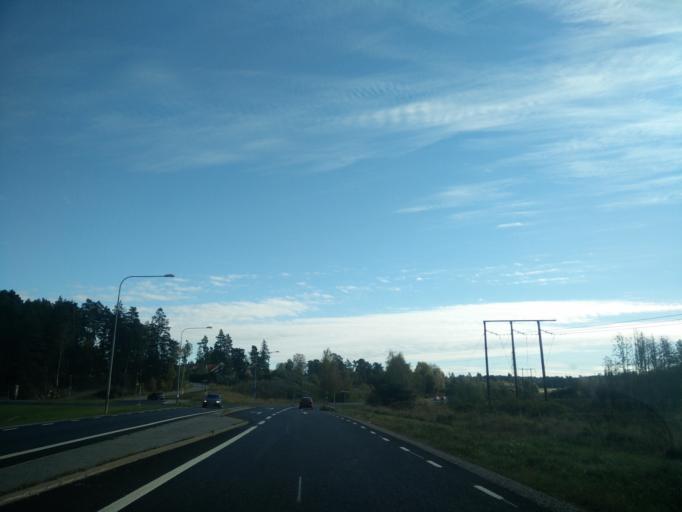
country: SE
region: Stockholm
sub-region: Upplands Vasby Kommun
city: Upplands Vaesby
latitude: 59.5101
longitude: 17.9611
